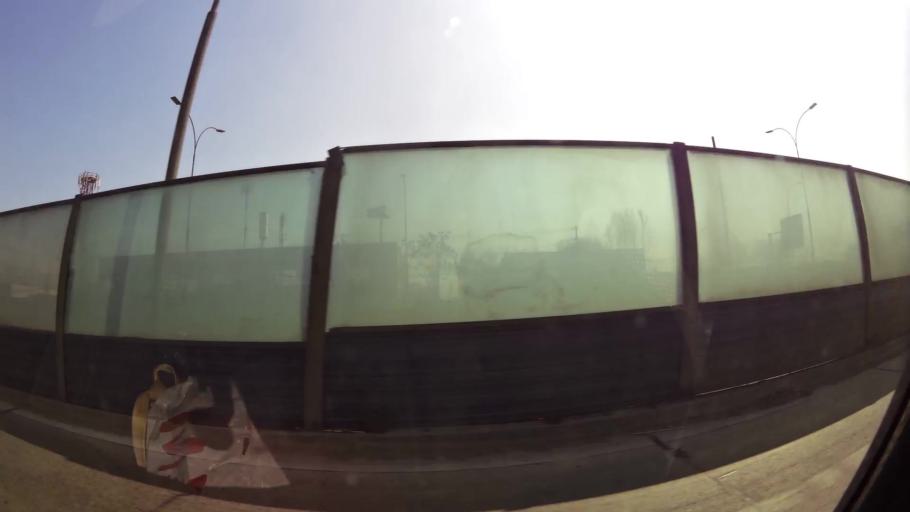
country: CL
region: Santiago Metropolitan
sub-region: Provincia de Santiago
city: Lo Prado
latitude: -33.4478
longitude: -70.6921
